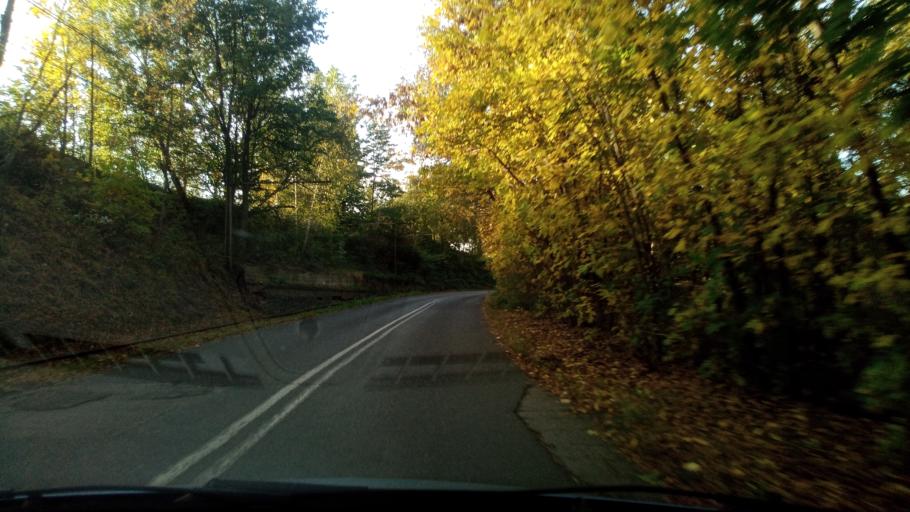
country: PL
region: Silesian Voivodeship
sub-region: Sosnowiec
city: Sosnowiec
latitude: 50.2534
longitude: 19.1223
